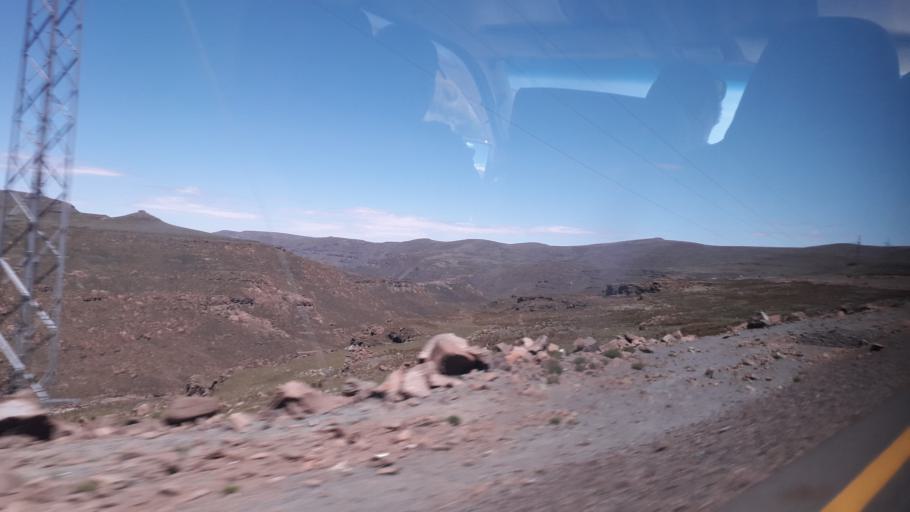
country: ZA
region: Orange Free State
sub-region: Thabo Mofutsanyana District Municipality
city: Phuthaditjhaba
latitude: -28.8365
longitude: 28.7462
